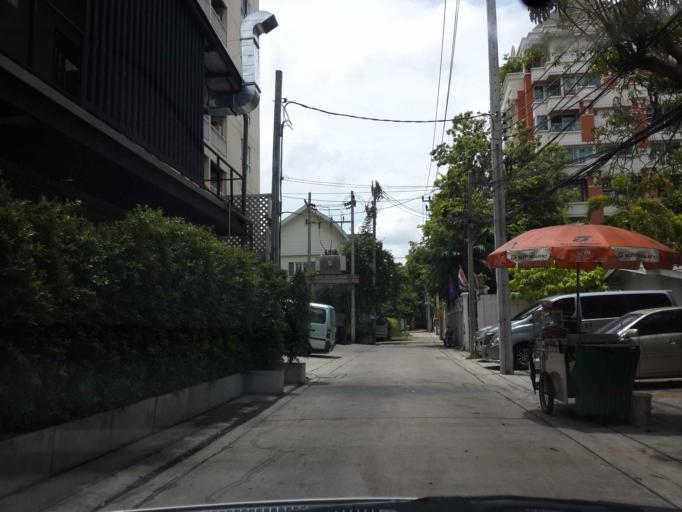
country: TH
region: Bangkok
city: Watthana
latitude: 13.7377
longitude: 100.5678
